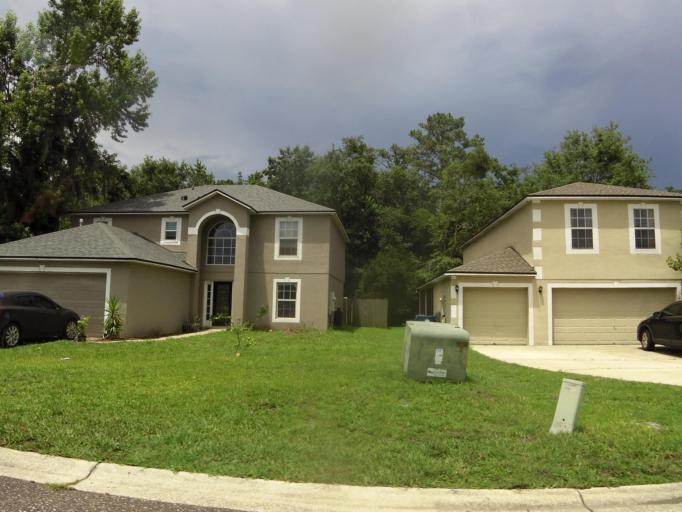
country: US
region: Florida
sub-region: Duval County
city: Jacksonville
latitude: 30.4259
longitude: -81.7257
